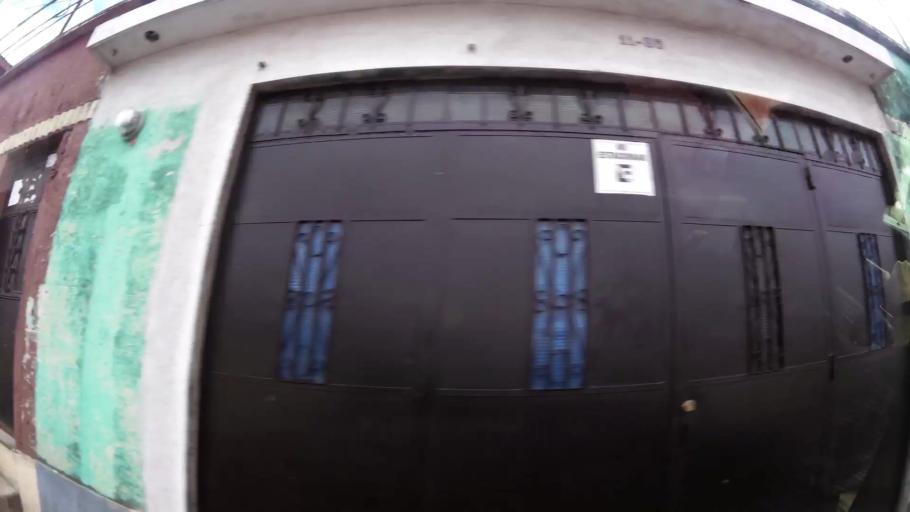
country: GT
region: Guatemala
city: Mixco
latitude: 14.6314
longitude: -90.6103
